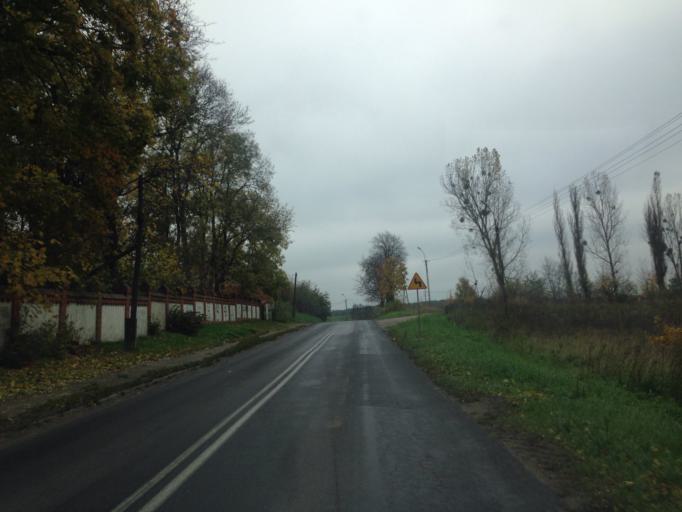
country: PL
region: Kujawsko-Pomorskie
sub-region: Powiat brodnicki
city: Jablonowo Pomorskie
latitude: 53.3441
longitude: 19.2137
